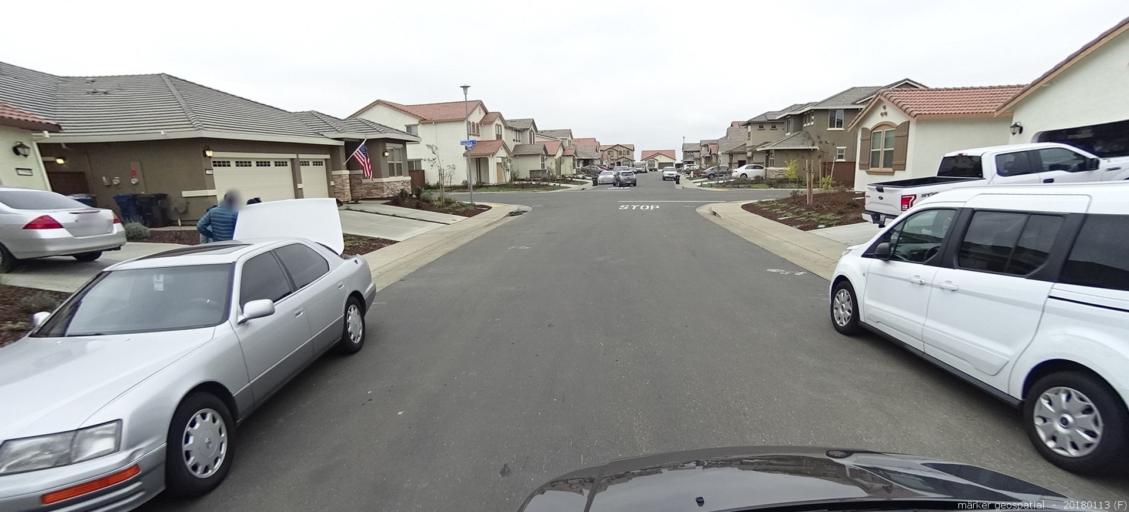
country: US
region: California
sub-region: Sacramento County
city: Gold River
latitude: 38.5673
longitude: -121.1999
